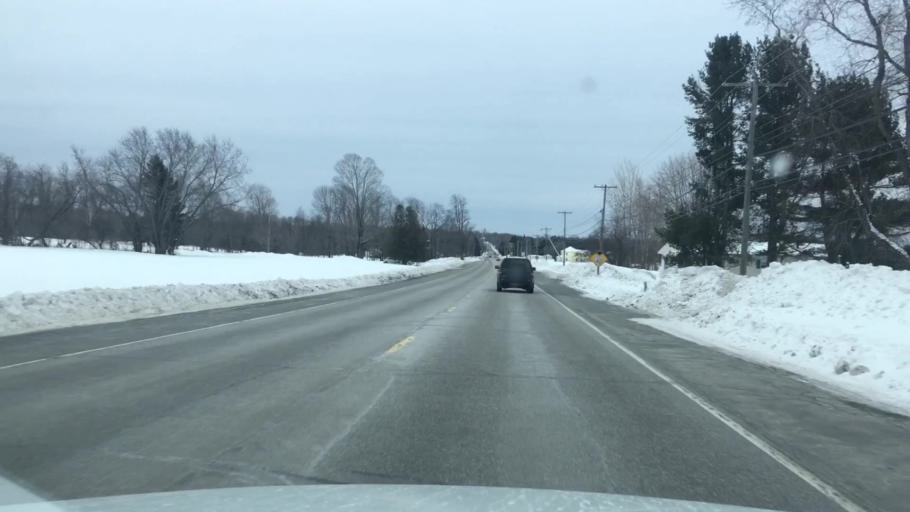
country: US
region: Maine
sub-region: Penobscot County
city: Charleston
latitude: 45.0222
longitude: -69.0294
